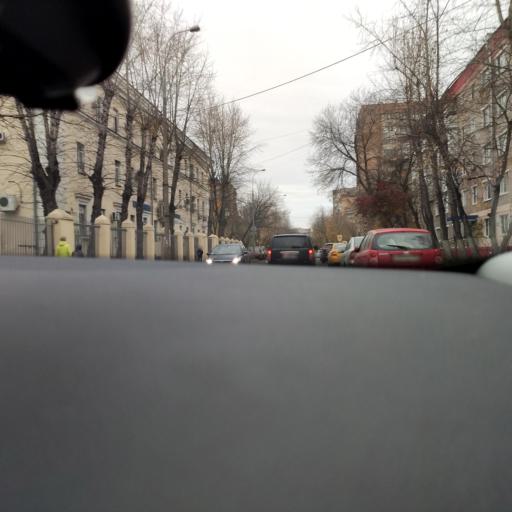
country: RU
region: Moscow
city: Tekstil'shchiki
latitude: 55.7002
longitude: 37.7426
